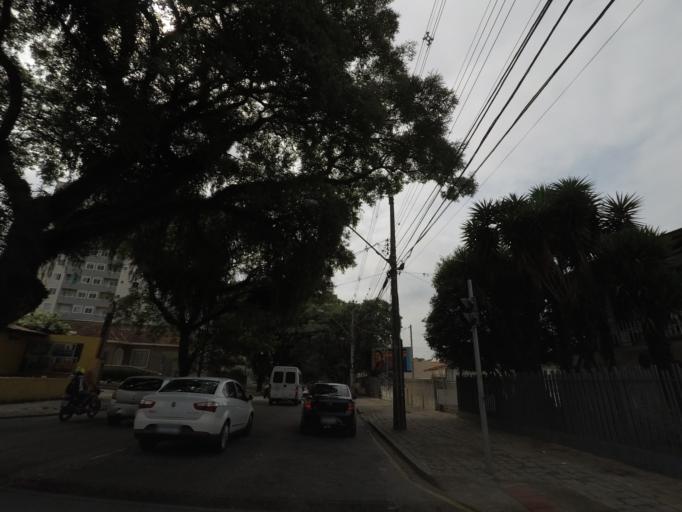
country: BR
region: Parana
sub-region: Curitiba
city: Curitiba
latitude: -25.4578
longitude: -49.2866
